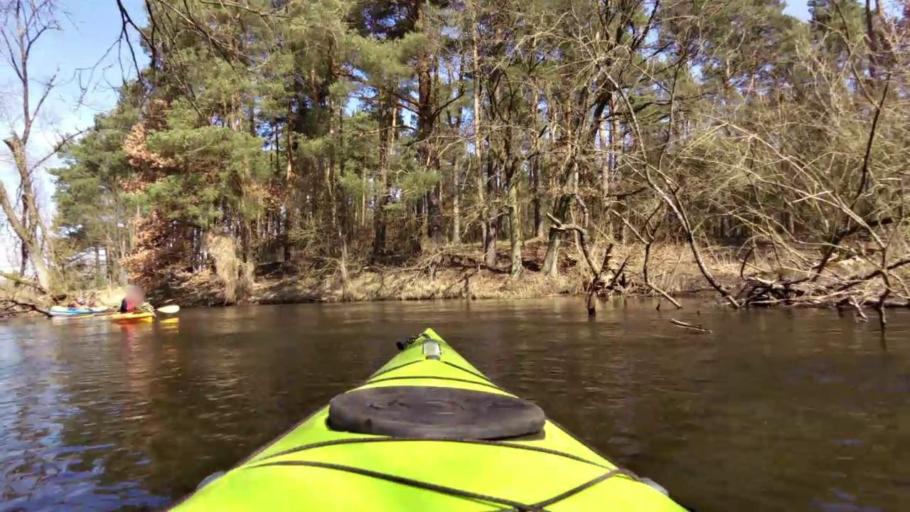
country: PL
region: West Pomeranian Voivodeship
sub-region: Powiat lobeski
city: Lobez
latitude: 53.6414
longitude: 15.5729
